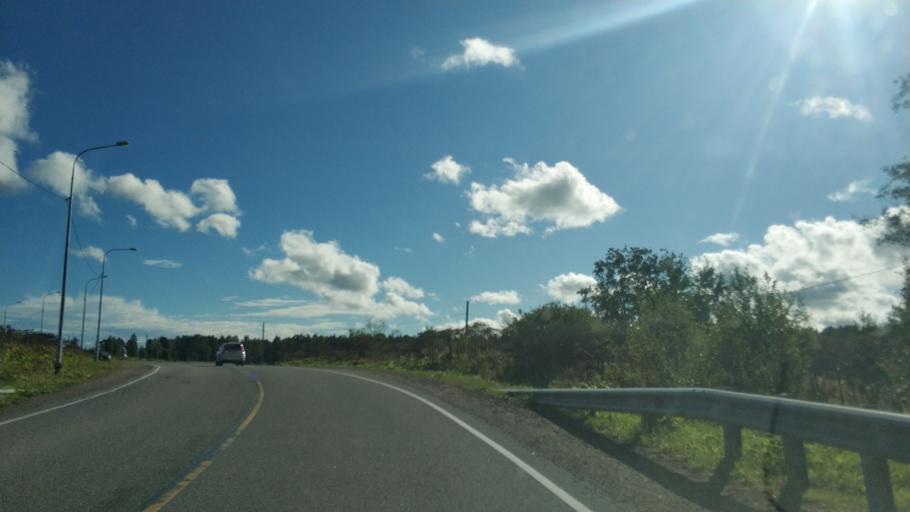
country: RU
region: Republic of Karelia
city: Khelyulya
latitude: 61.6457
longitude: 30.5828
